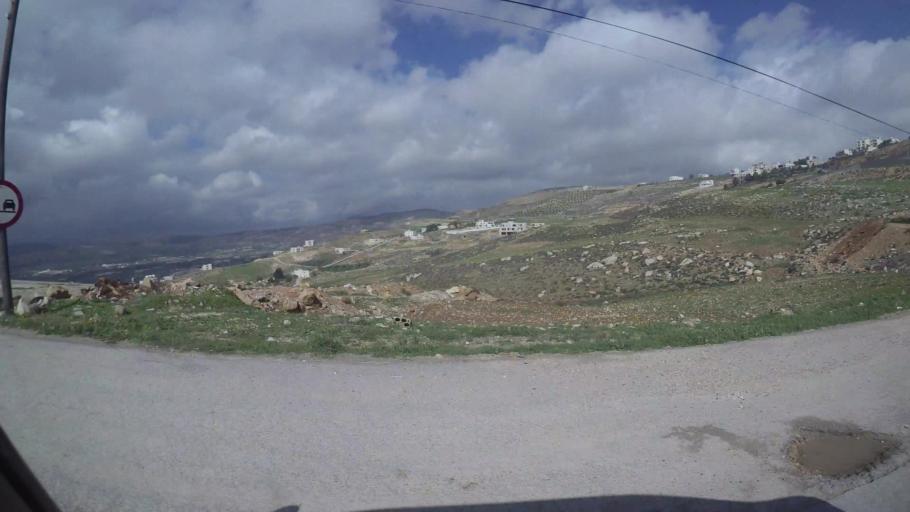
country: JO
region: Amman
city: Al Jubayhah
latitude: 32.0721
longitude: 35.8725
